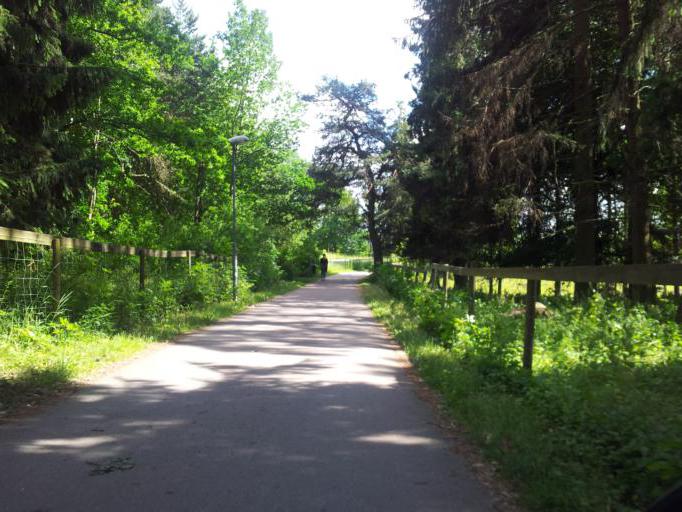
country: SE
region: Uppsala
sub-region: Uppsala Kommun
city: Uppsala
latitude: 59.8797
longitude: 17.6709
